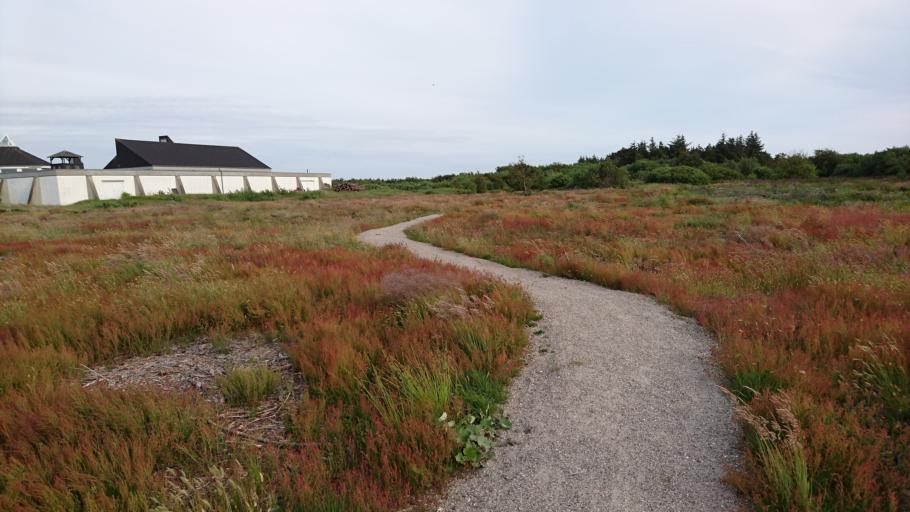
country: DK
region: North Denmark
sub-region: Frederikshavn Kommune
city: Skagen
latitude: 57.7406
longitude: 10.5936
